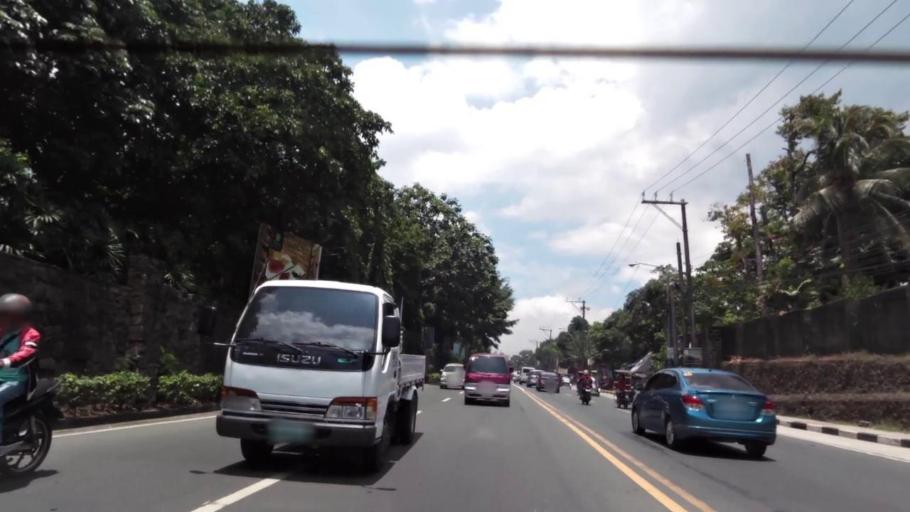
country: PH
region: Calabarzon
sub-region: Province of Rizal
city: Antipolo
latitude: 14.6041
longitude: 121.1748
